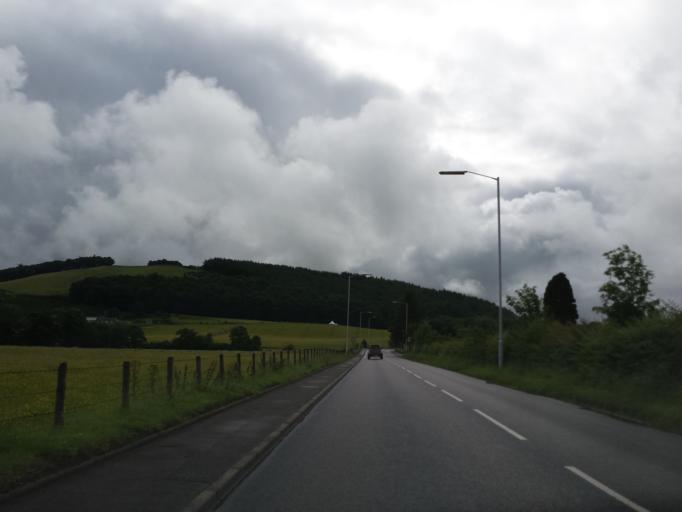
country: GB
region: Scotland
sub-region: Fife
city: Newburgh
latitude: 56.3503
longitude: -3.2276
